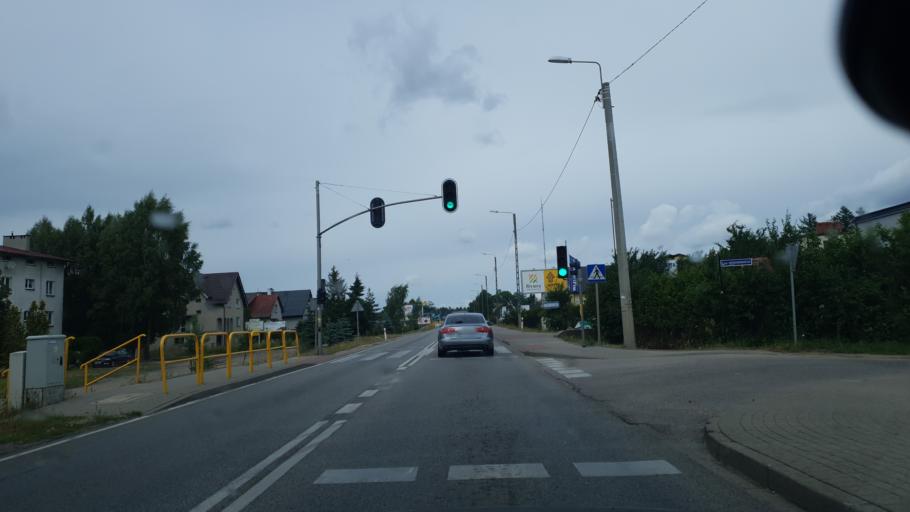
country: PL
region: Pomeranian Voivodeship
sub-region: Powiat kartuski
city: Chwaszczyno
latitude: 54.4401
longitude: 18.4144
